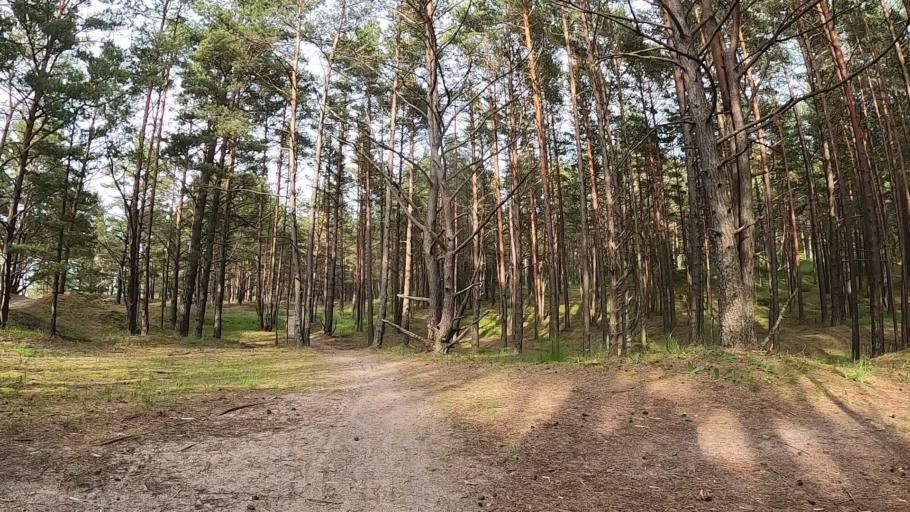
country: LV
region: Riga
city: Jaunciems
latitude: 57.0931
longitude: 24.1422
